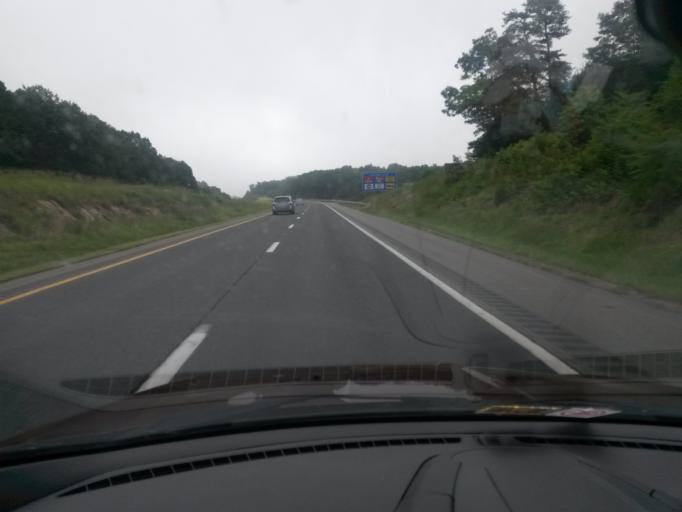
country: US
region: Virginia
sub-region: Campbell County
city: Timberlake
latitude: 37.3190
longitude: -79.2210
